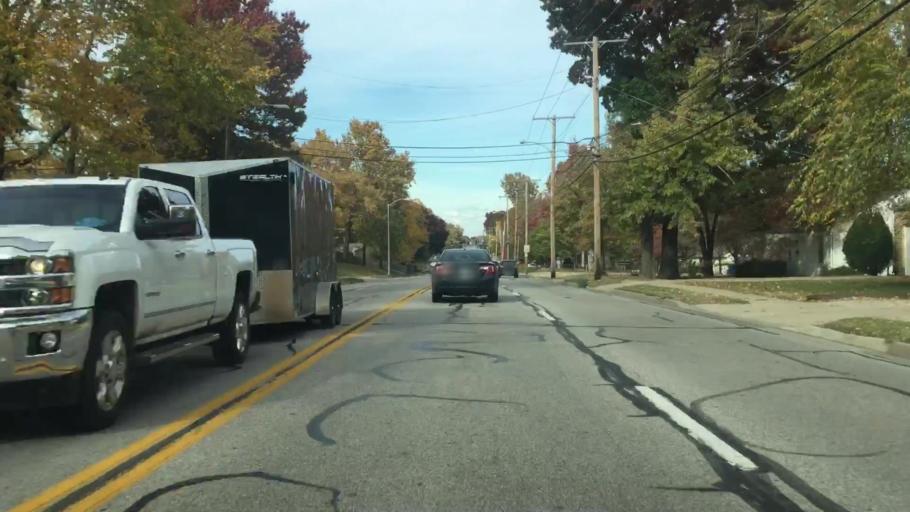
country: US
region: Kansas
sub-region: Johnson County
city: Merriam
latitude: 39.0044
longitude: -94.7238
